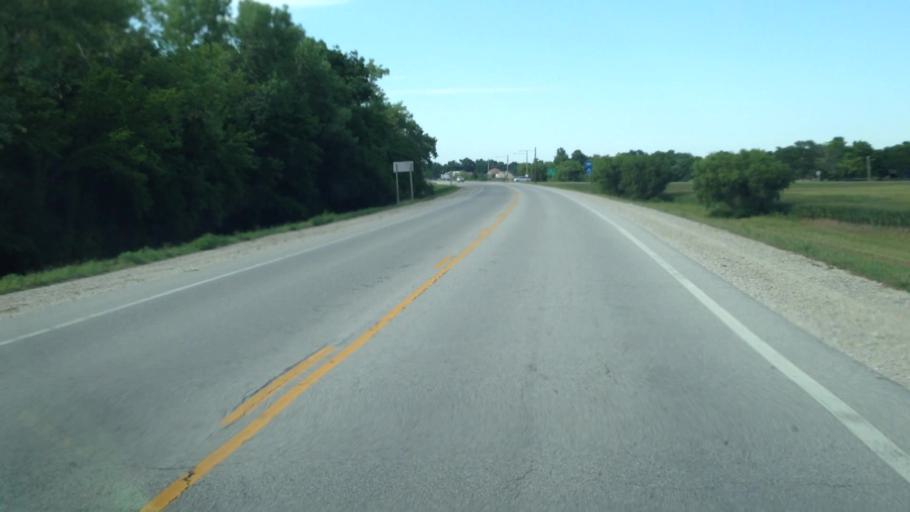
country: US
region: Kansas
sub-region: Neosho County
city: Erie
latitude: 37.5626
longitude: -95.2535
